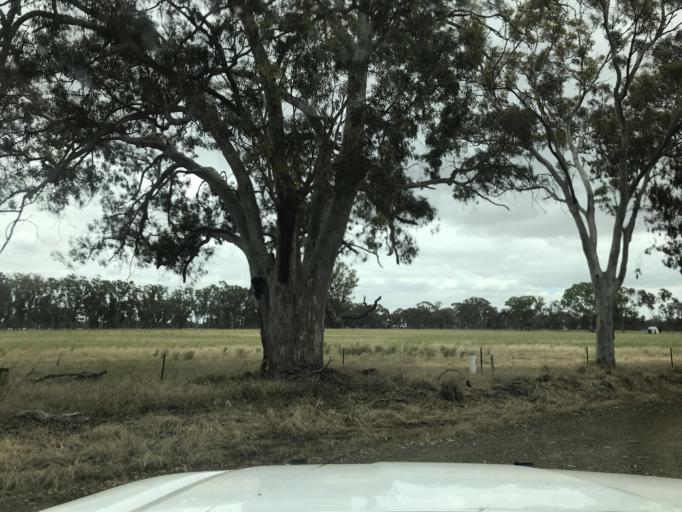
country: AU
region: South Australia
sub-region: Naracoorte and Lucindale
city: Naracoorte
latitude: -36.9497
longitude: 141.3121
